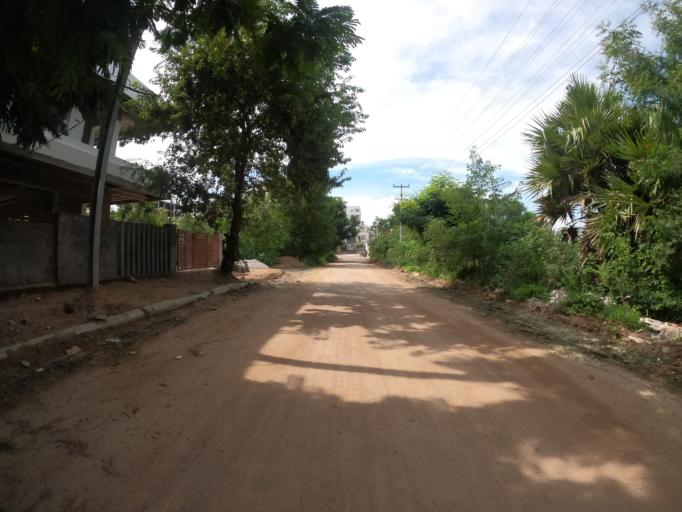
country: IN
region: Telangana
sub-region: Hyderabad
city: Hyderabad
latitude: 17.3535
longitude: 78.3975
